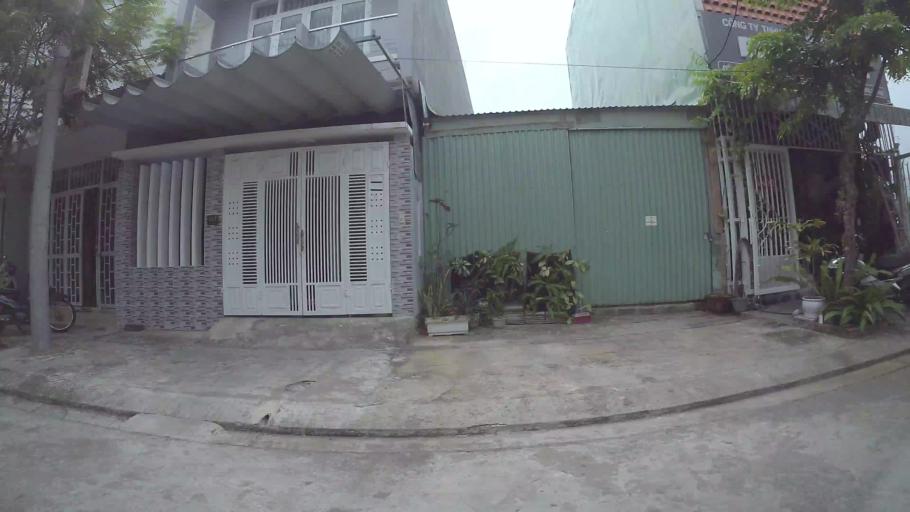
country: VN
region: Da Nang
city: Lien Chieu
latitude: 16.0739
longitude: 108.1679
